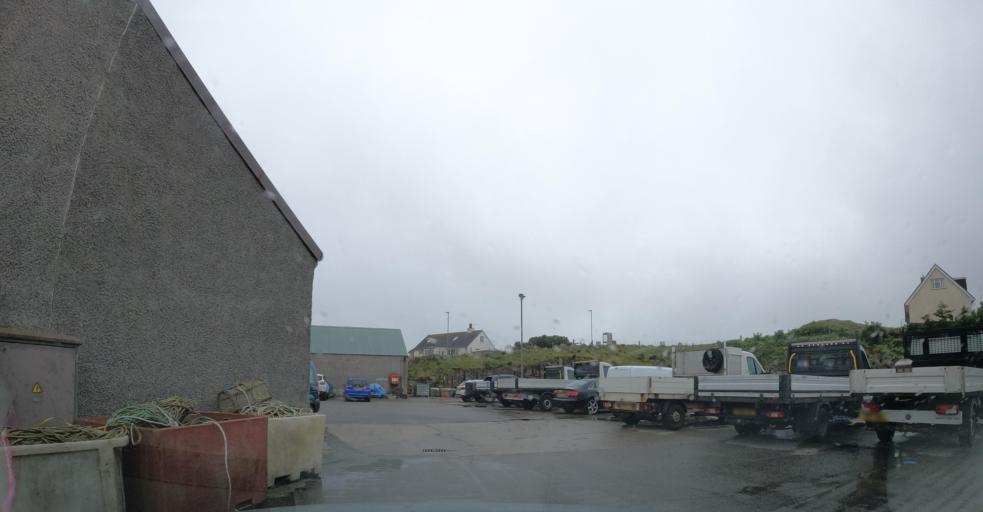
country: GB
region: Scotland
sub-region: Eilean Siar
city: Benbecula
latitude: 57.4812
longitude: -7.2046
